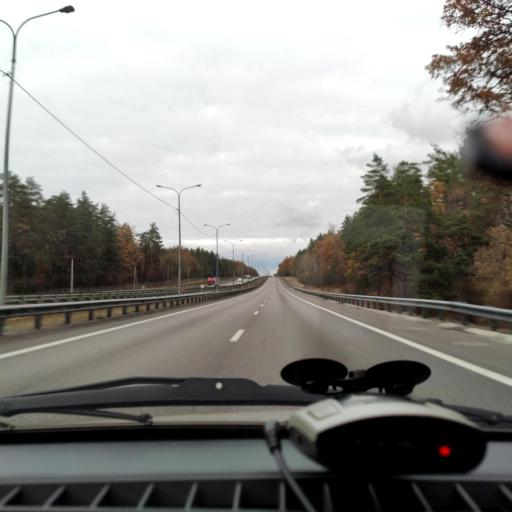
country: RU
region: Voronezj
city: Ramon'
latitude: 51.8688
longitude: 39.2165
